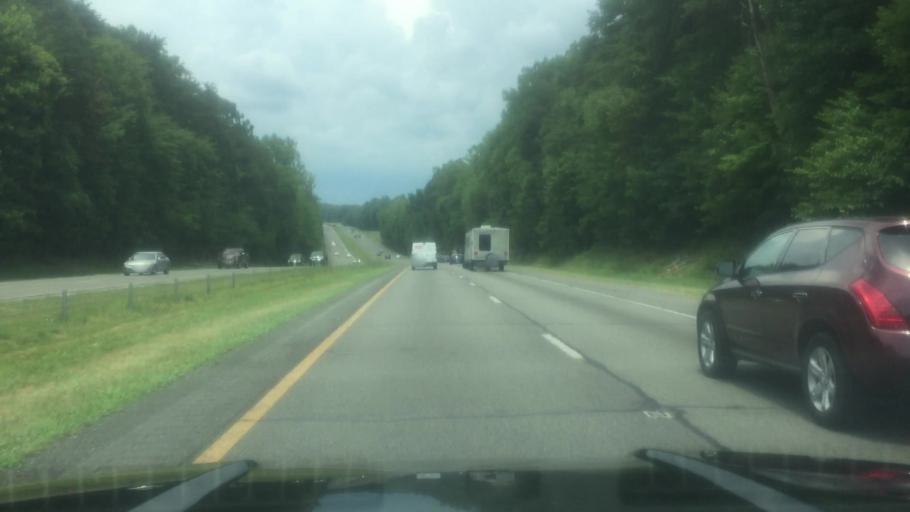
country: US
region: North Carolina
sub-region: Surry County
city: Pilot Mountain
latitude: 36.3321
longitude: -80.4531
